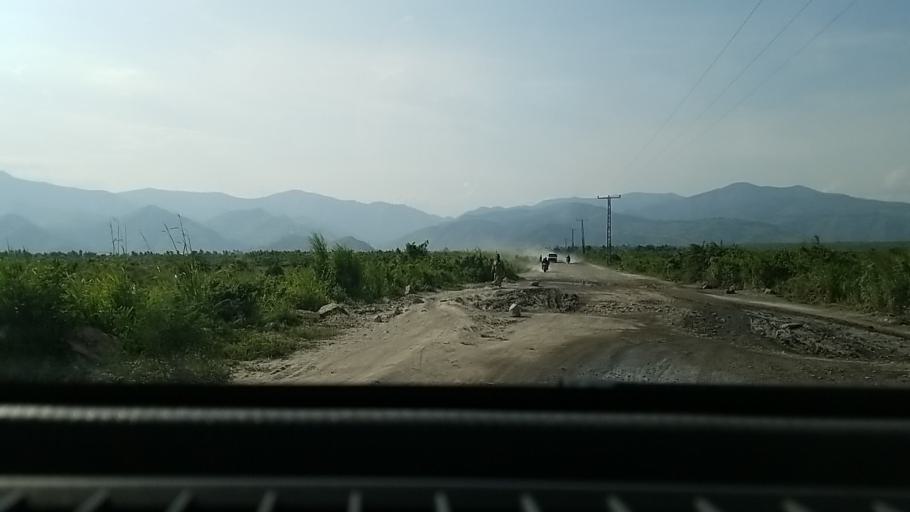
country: CD
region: Nord Kivu
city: Sake
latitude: -1.5819
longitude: 29.0815
